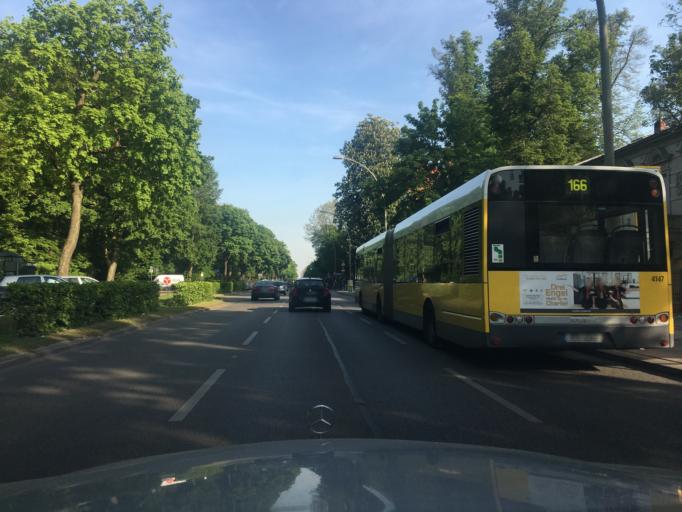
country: DE
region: Berlin
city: Treptow Bezirk
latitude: 52.4877
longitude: 13.4635
